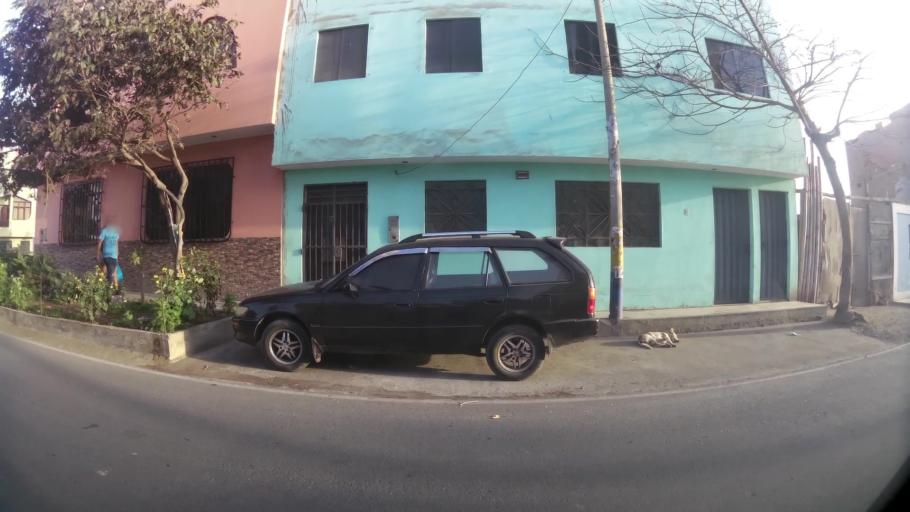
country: PE
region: Lima
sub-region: Huaura
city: Hualmay
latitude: -11.0989
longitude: -77.6109
